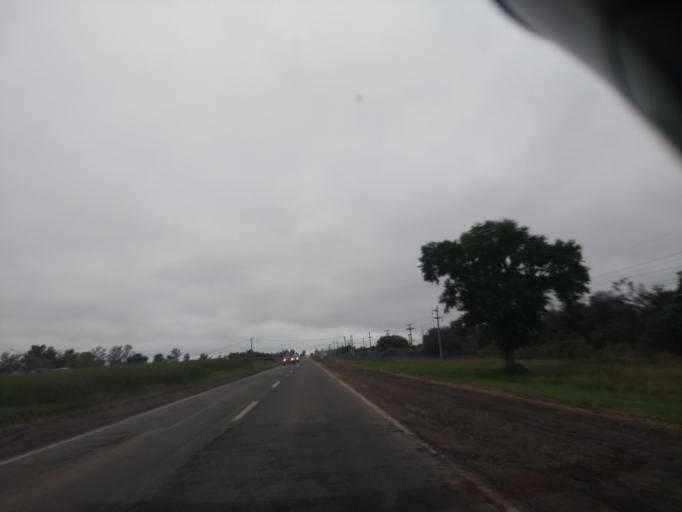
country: AR
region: Chaco
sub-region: Departamento de Quitilipi
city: Quitilipi
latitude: -26.8735
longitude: -60.2458
